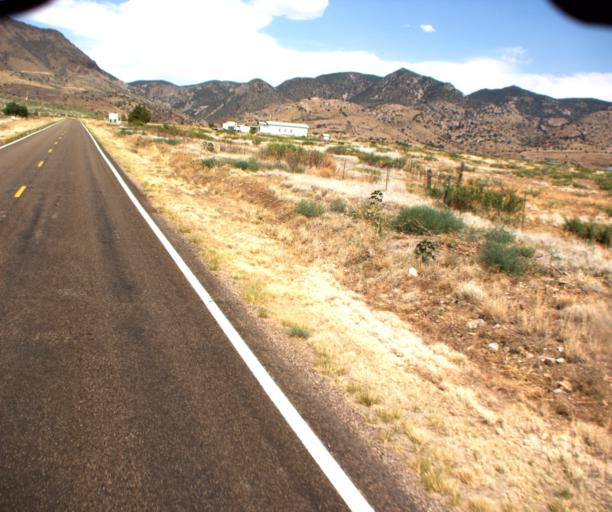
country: US
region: Arizona
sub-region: Greenlee County
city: Clifton
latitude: 33.0382
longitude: -109.1255
